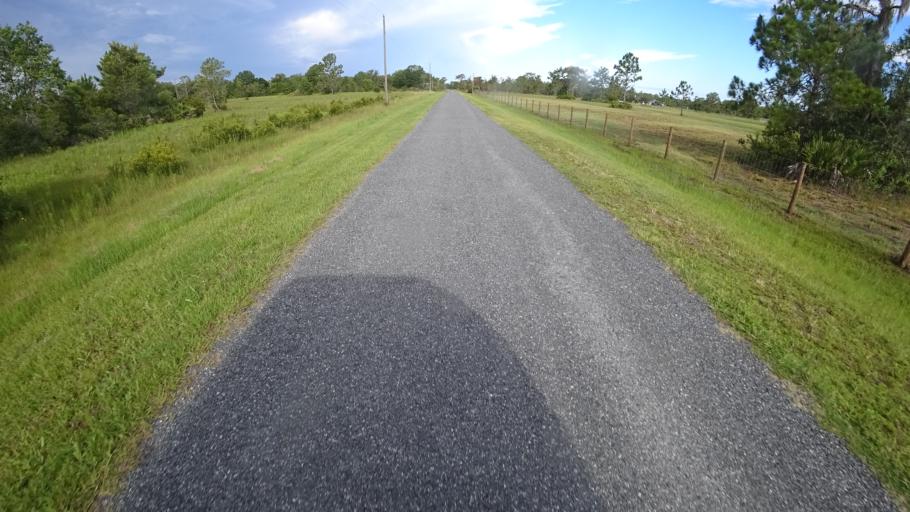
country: US
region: Florida
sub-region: Sarasota County
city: Fruitville
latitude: 27.4088
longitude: -82.2819
